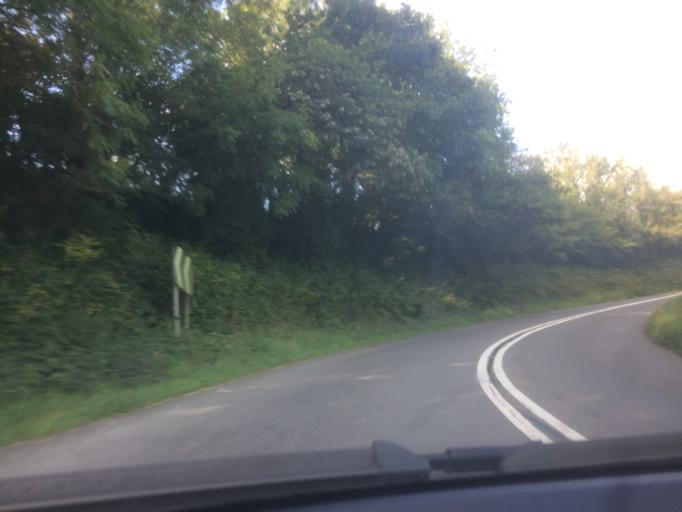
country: GB
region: England
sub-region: Devon
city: Tavistock
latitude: 50.5351
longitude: -4.1757
